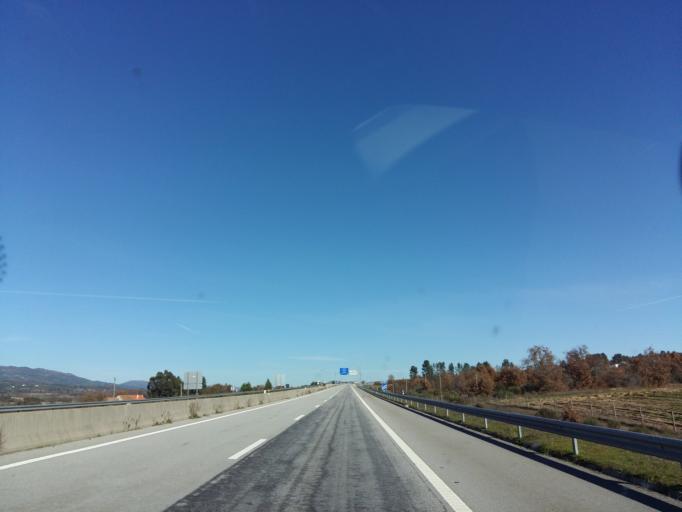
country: PT
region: Castelo Branco
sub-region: Covilha
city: Teixoso
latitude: 40.2582
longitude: -7.4441
